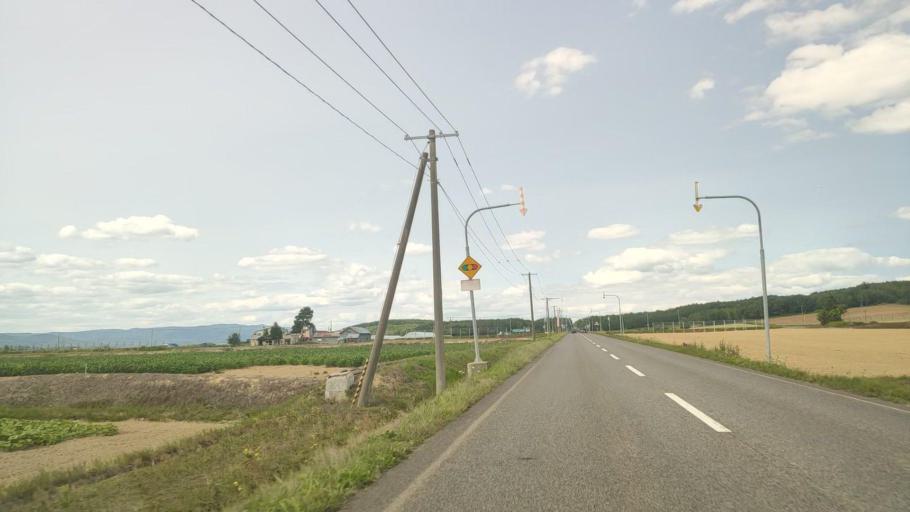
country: JP
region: Hokkaido
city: Nayoro
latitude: 44.2333
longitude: 142.4157
